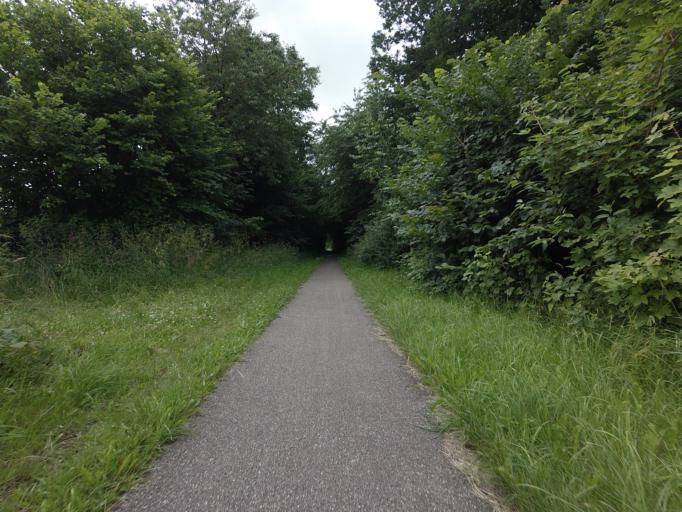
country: DK
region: Central Jutland
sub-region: Randers Kommune
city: Langa
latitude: 56.3236
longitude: 9.8816
